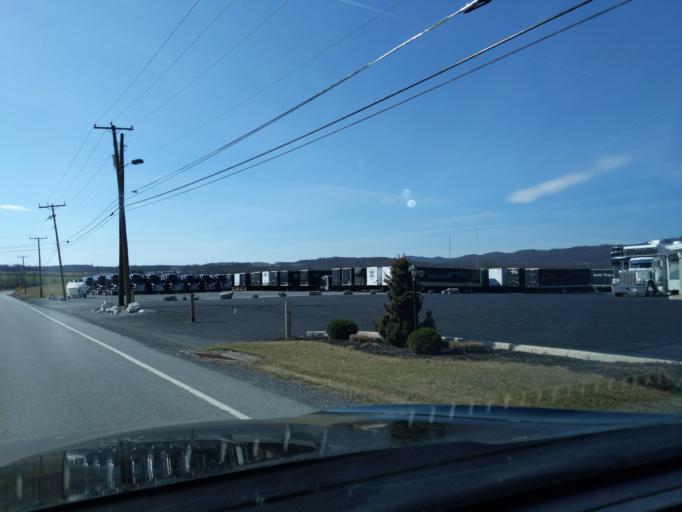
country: US
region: Pennsylvania
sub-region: Blair County
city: Roaring Spring
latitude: 40.3271
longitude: -78.3903
